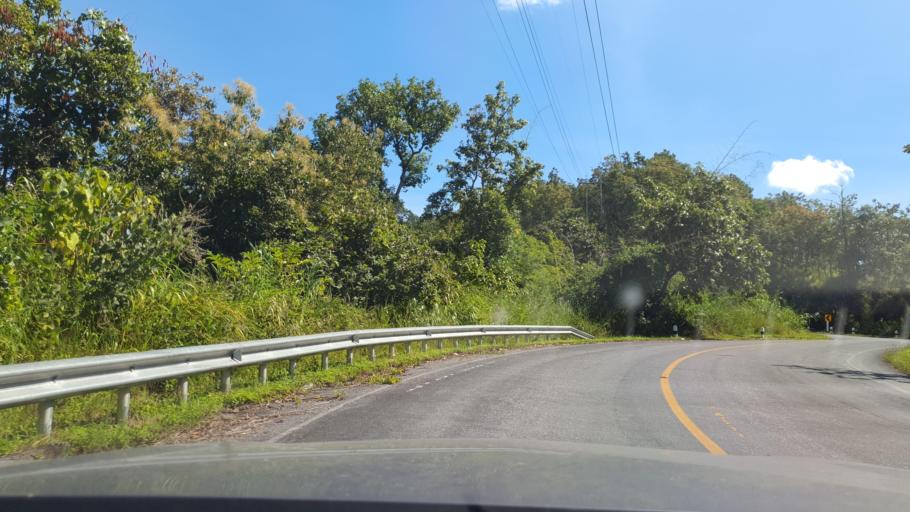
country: TH
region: Chiang Mai
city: Phrao
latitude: 19.3564
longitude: 99.2737
